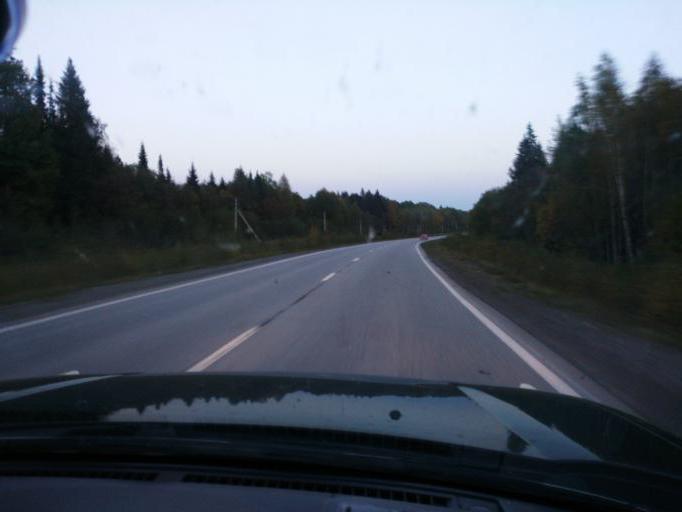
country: RU
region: Perm
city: Verkhnechusovskiye Gorodki
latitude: 58.2568
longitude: 56.9968
